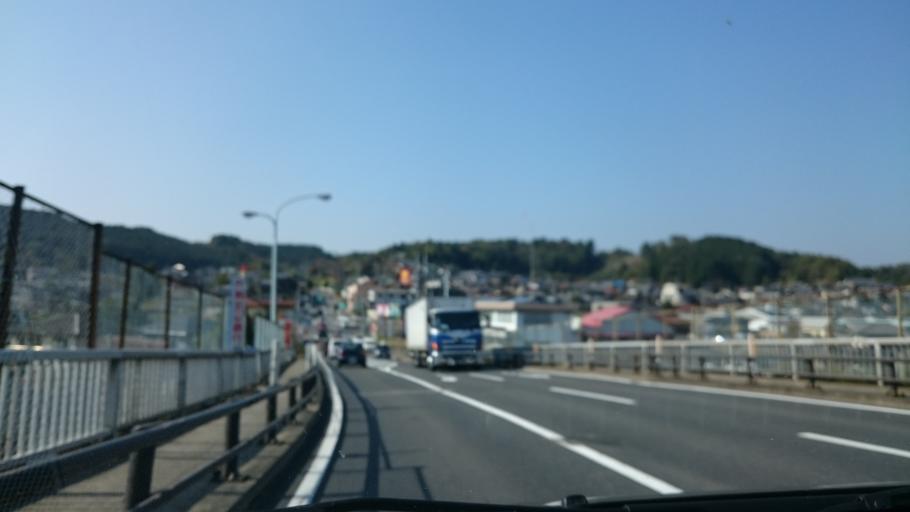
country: JP
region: Gifu
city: Nakatsugawa
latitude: 35.4922
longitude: 137.4889
